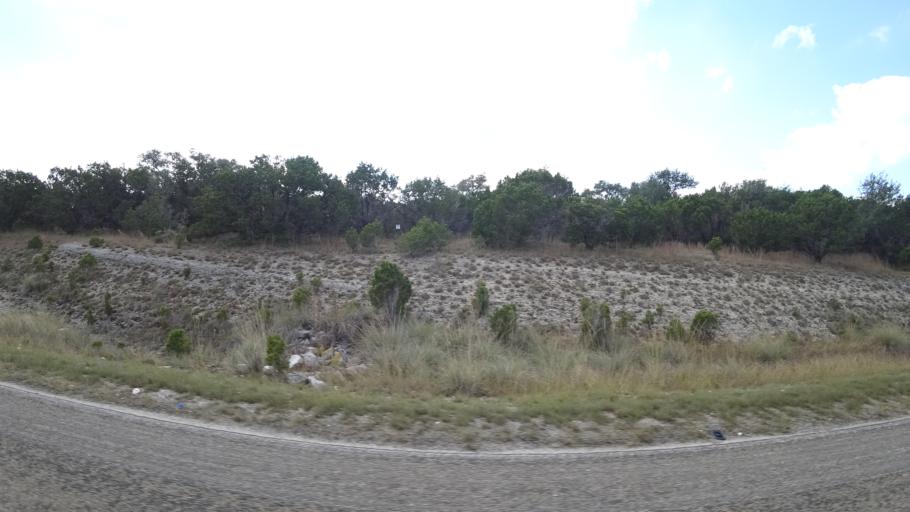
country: US
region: Texas
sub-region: Travis County
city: Barton Creek
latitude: 30.2802
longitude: -97.9046
